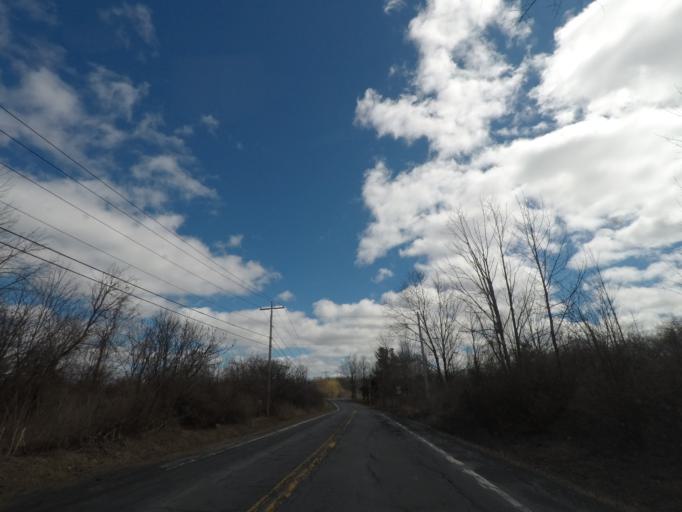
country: US
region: New York
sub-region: Albany County
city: Altamont
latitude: 42.6726
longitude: -74.0713
